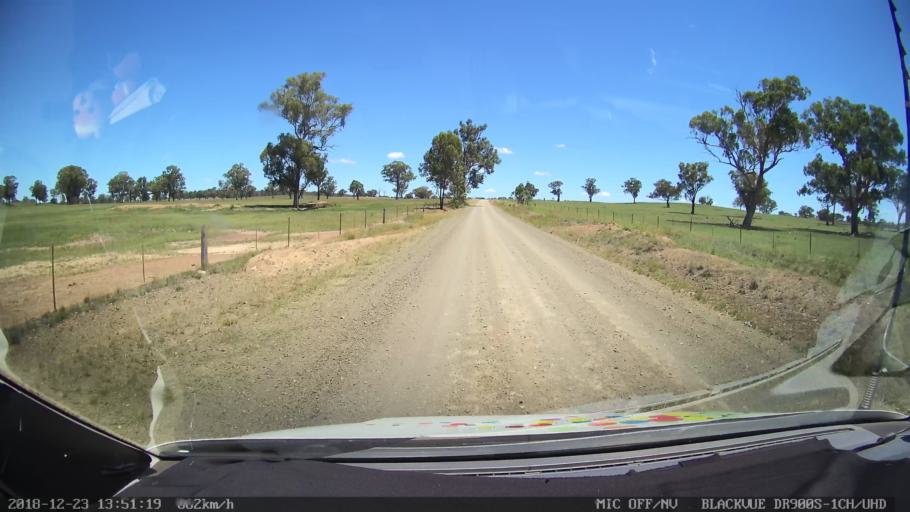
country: AU
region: New South Wales
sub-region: Tamworth Municipality
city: Manilla
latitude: -30.5387
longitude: 151.1053
